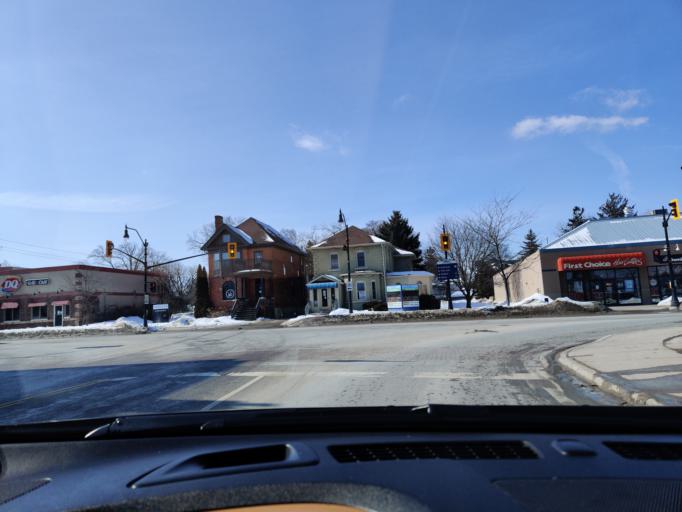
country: CA
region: Ontario
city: Collingwood
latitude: 44.4955
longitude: -80.2156
